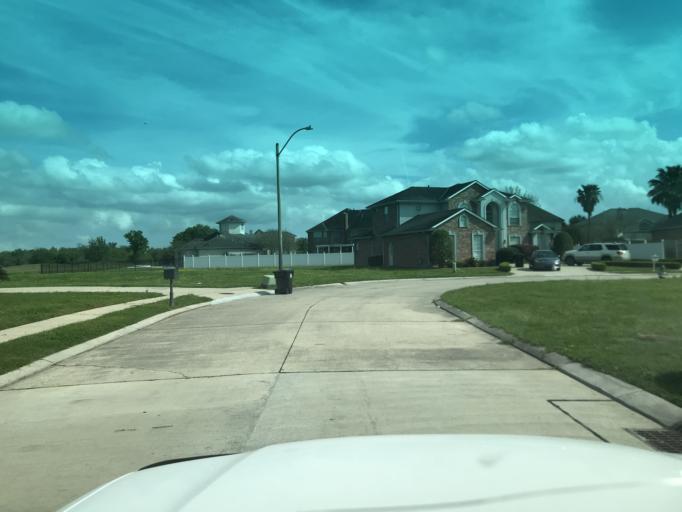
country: US
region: Louisiana
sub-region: Saint Bernard Parish
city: Chalmette
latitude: 30.0366
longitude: -89.9504
